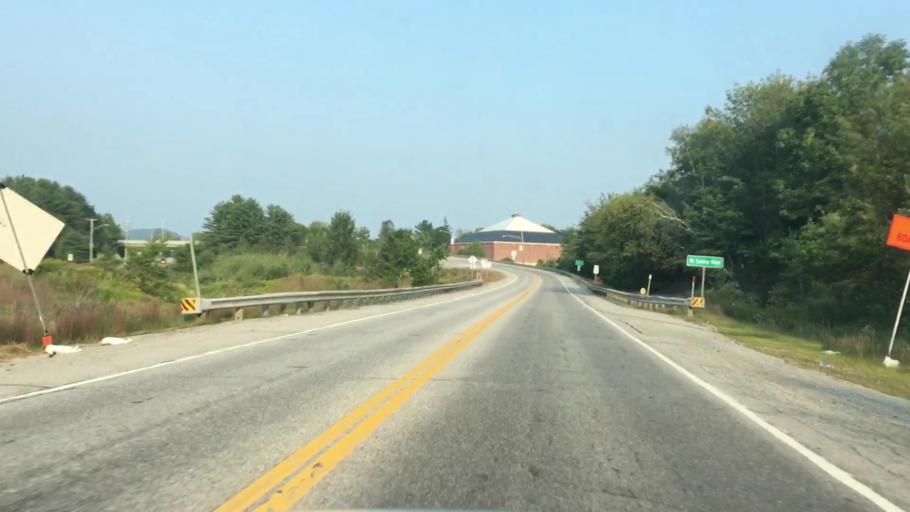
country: US
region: Maine
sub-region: Oxford County
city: Bethel
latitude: 44.4094
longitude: -70.8003
